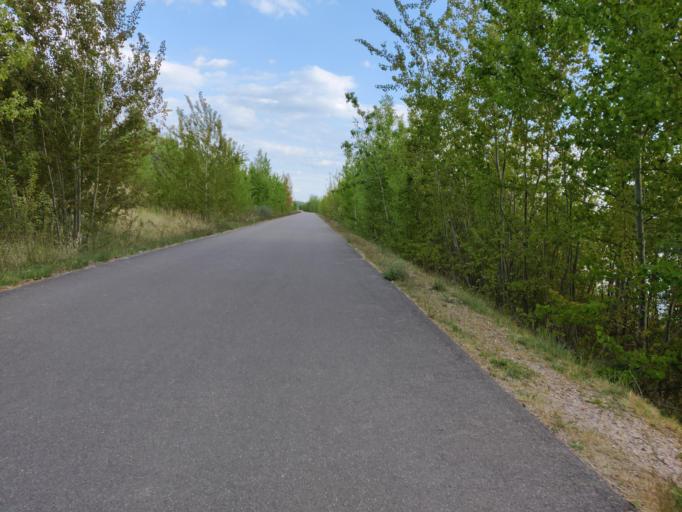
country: DE
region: Saxony
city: Rotha
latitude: 51.2263
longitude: 12.4373
